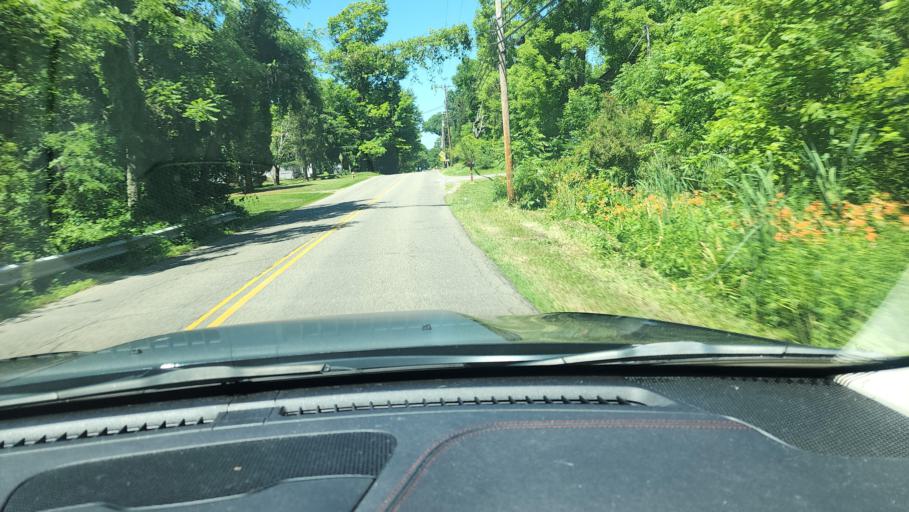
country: US
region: Ohio
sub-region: Mahoning County
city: Austintown
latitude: 41.0921
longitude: -80.7917
